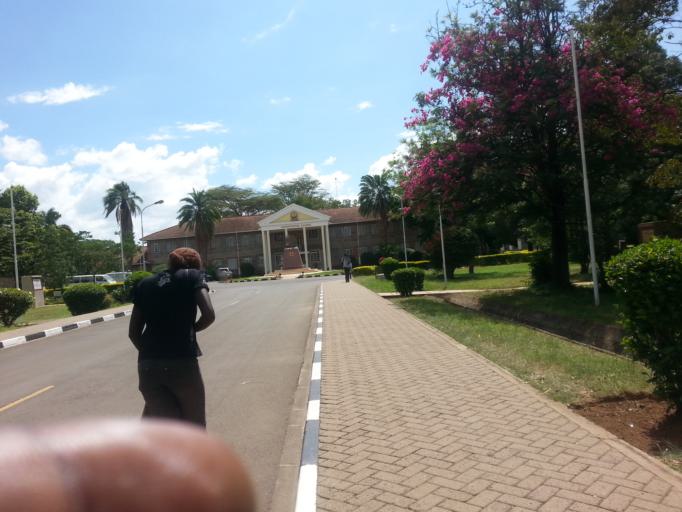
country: KE
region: Nakuru
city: Rongai
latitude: -0.1664
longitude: 35.9667
